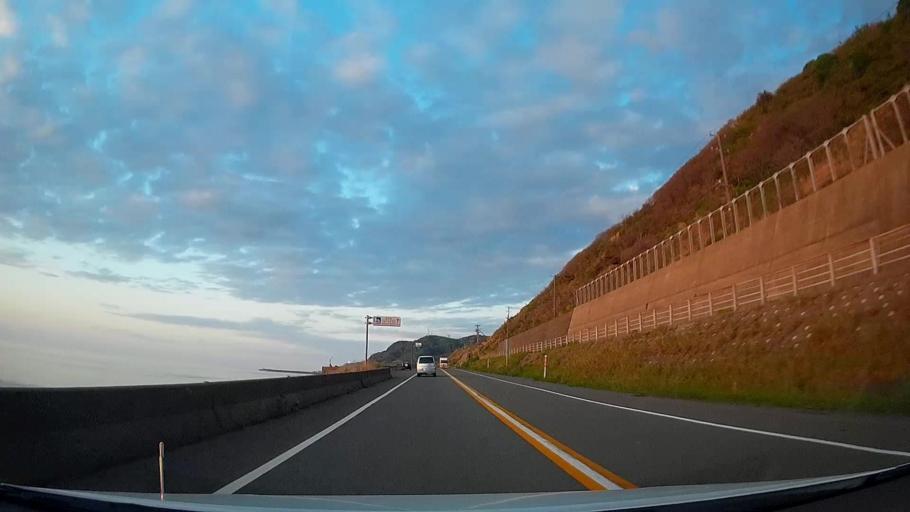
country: JP
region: Niigata
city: Joetsu
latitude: 37.1497
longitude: 138.0704
